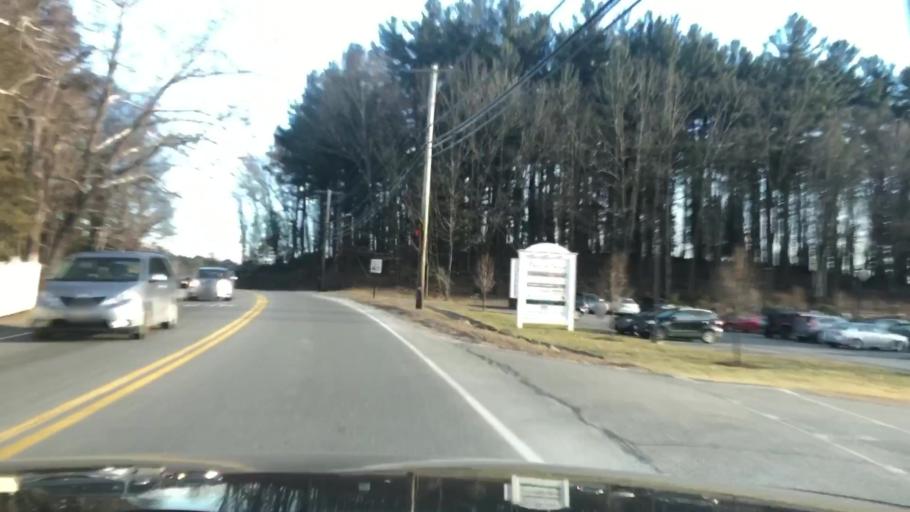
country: US
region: Massachusetts
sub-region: Worcester County
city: Bolton
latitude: 42.4322
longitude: -71.6027
